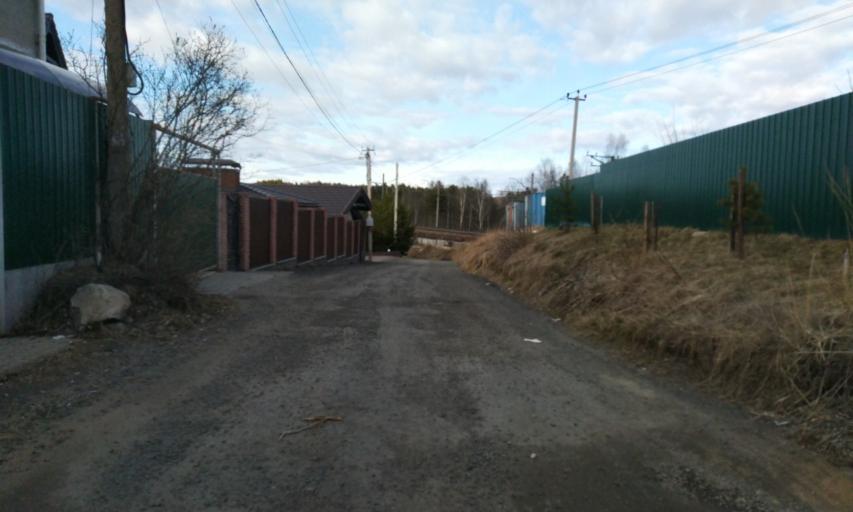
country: RU
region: Leningrad
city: Toksovo
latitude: 60.1241
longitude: 30.4884
